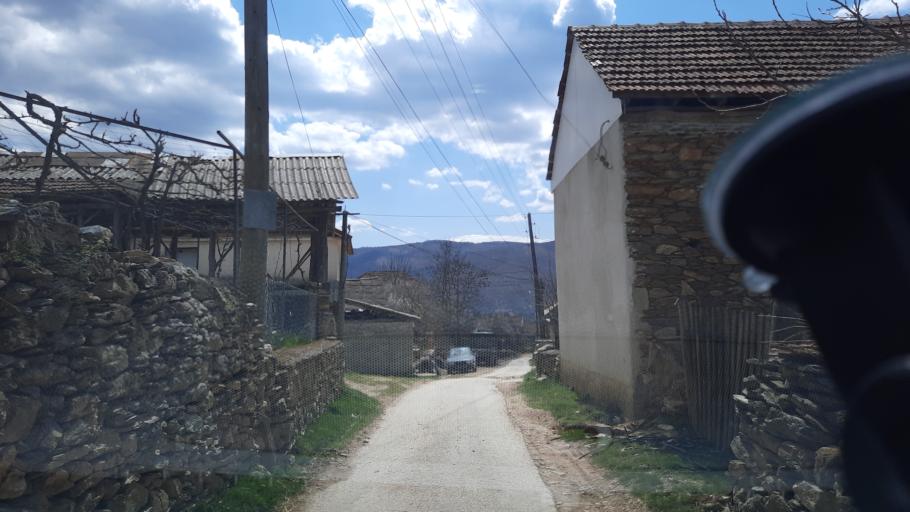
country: MK
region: Demir Hisar
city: Sopotnica
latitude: 41.3013
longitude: 21.1527
